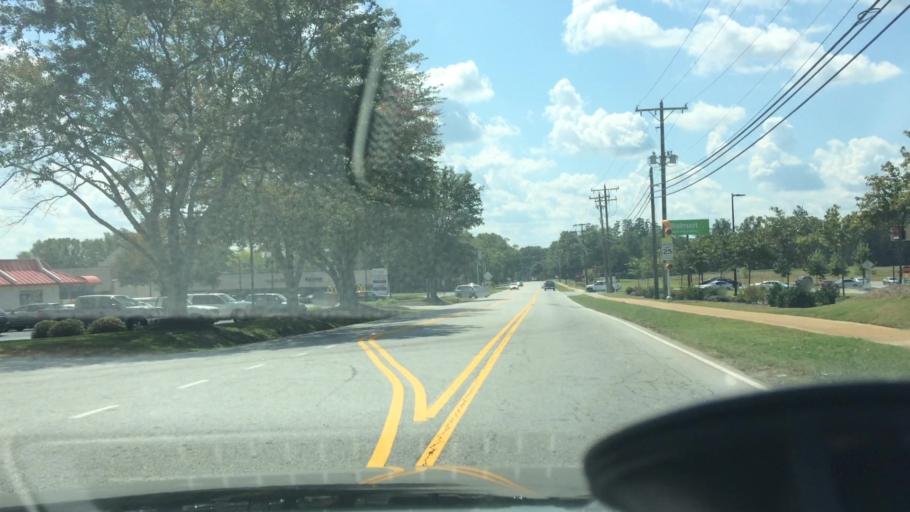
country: US
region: South Carolina
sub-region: Greenville County
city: Sans Souci
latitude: 34.9126
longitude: -82.4293
